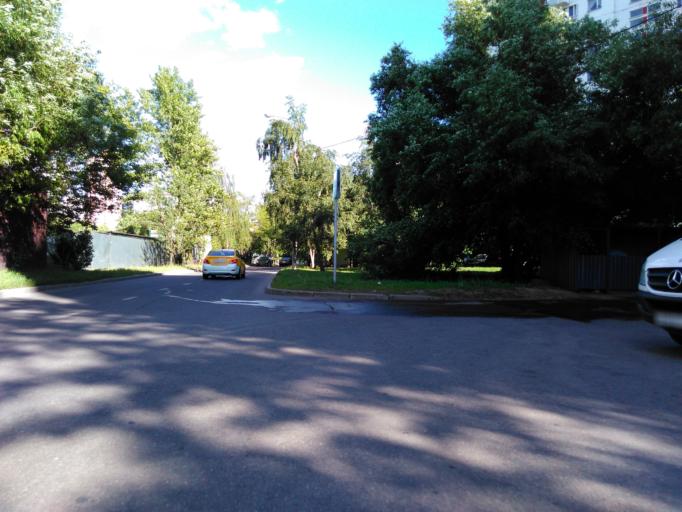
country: RU
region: Moscow
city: Troparevo
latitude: 55.6668
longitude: 37.4991
